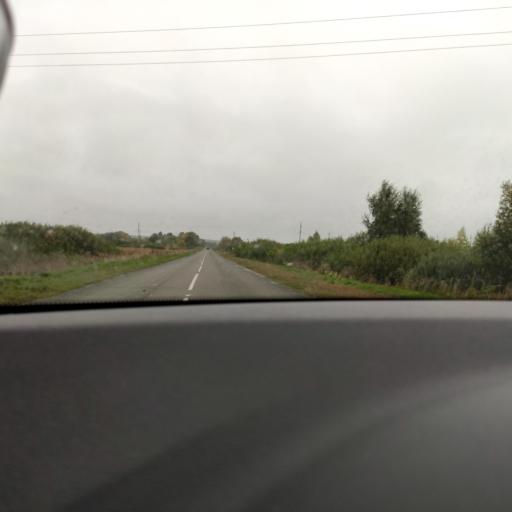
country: RU
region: Samara
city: Yelkhovka
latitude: 53.7386
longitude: 50.3081
